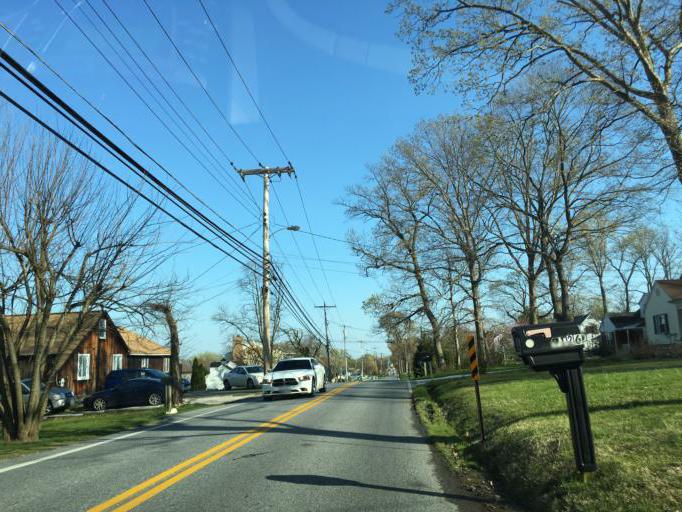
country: US
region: Maryland
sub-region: Baltimore County
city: Perry Hall
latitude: 39.4028
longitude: -76.4912
